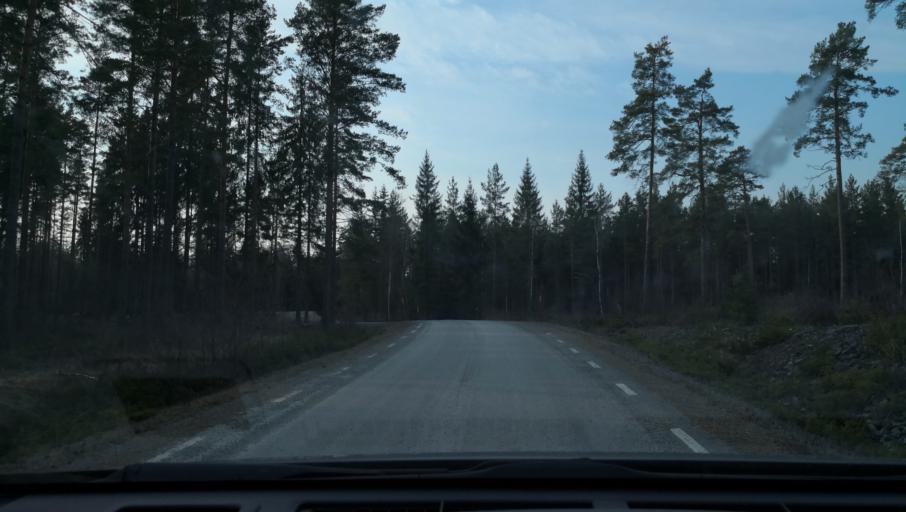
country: SE
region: OErebro
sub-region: Lindesbergs Kommun
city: Frovi
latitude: 59.3711
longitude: 15.3212
